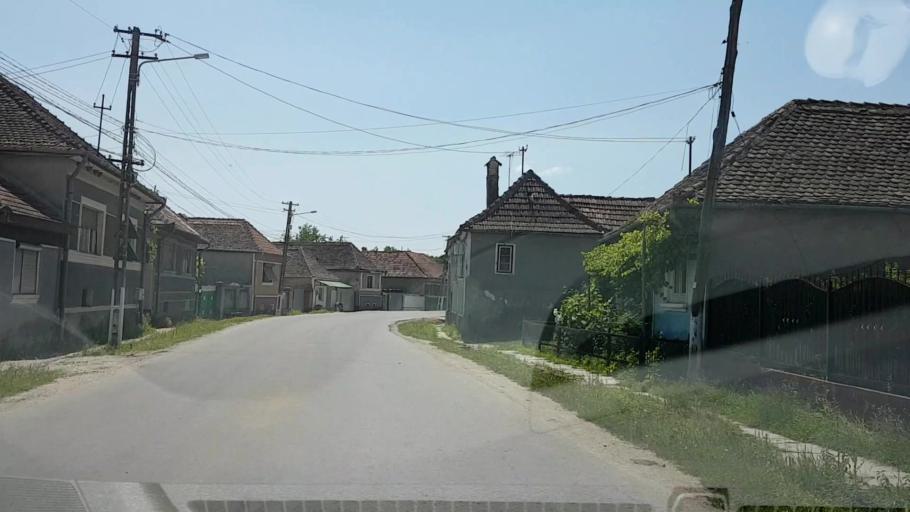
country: RO
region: Brasov
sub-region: Comuna Cincu
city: Cincu
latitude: 45.9126
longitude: 24.8076
